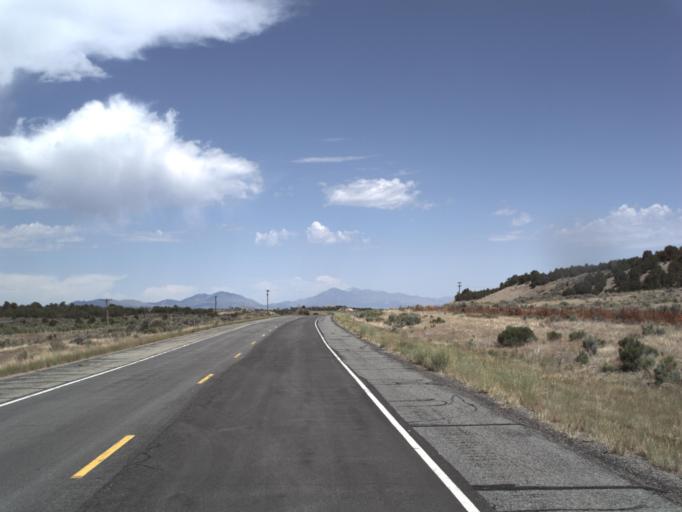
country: US
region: Utah
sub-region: Utah County
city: Genola
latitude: 39.9662
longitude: -112.2526
